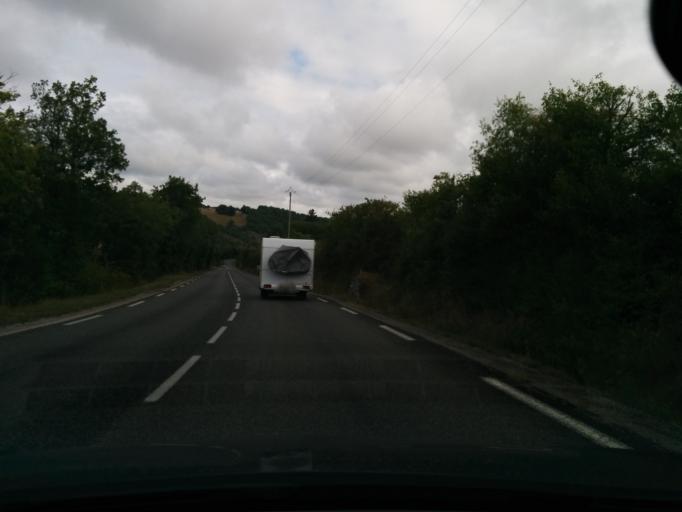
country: FR
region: Midi-Pyrenees
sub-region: Departement du Lot
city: Le Vigan
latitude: 44.6485
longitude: 1.4798
